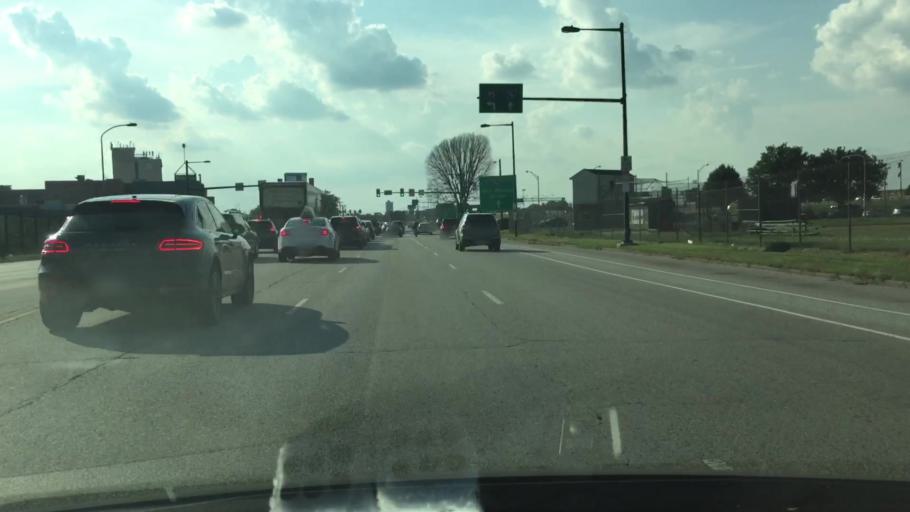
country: US
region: Pennsylvania
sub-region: Philadelphia County
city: Philadelphia
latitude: 39.9086
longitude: -75.1603
